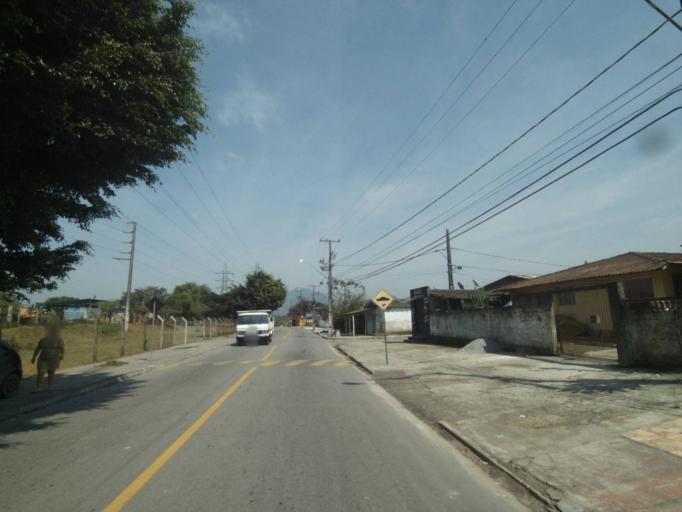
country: BR
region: Parana
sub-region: Paranagua
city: Paranagua
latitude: -25.5449
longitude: -48.5498
